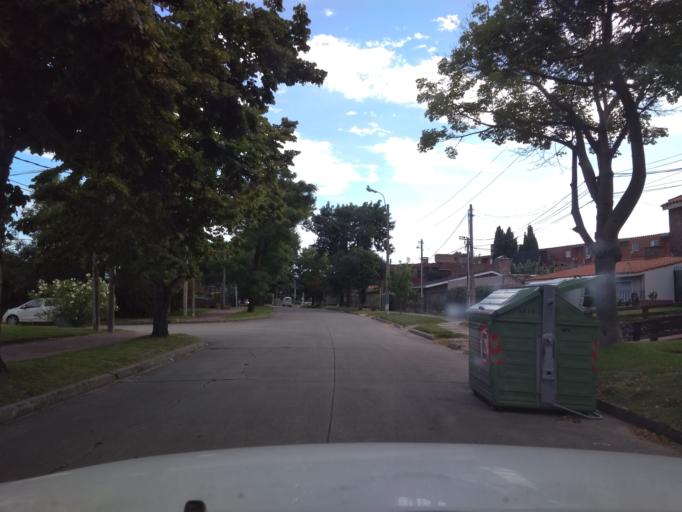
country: UY
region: Canelones
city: Paso de Carrasco
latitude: -34.8875
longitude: -56.0842
